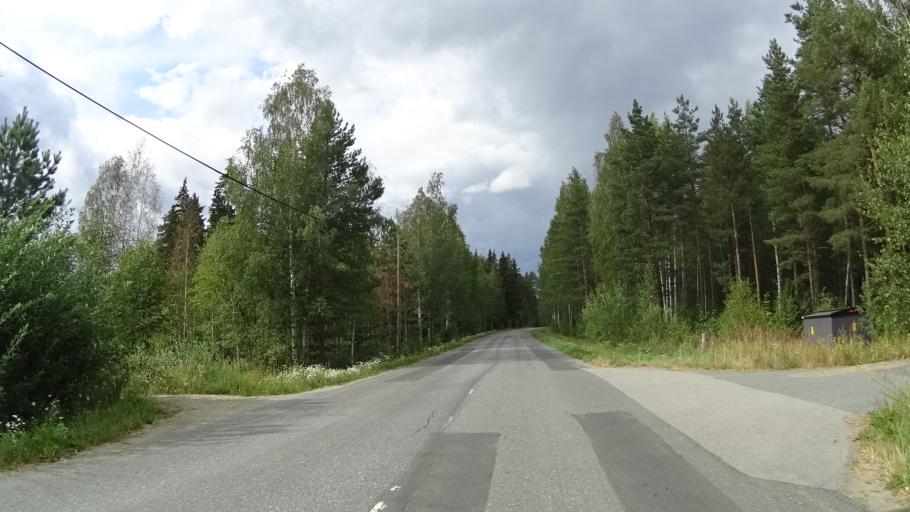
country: FI
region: Pirkanmaa
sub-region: Tampere
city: Kangasala
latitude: 61.4489
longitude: 24.1200
